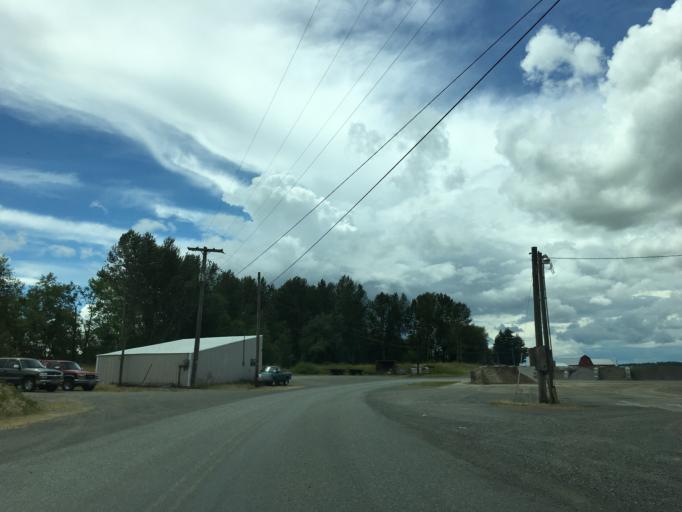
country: US
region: Washington
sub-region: Whatcom County
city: Lynden
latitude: 48.9190
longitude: -122.4882
